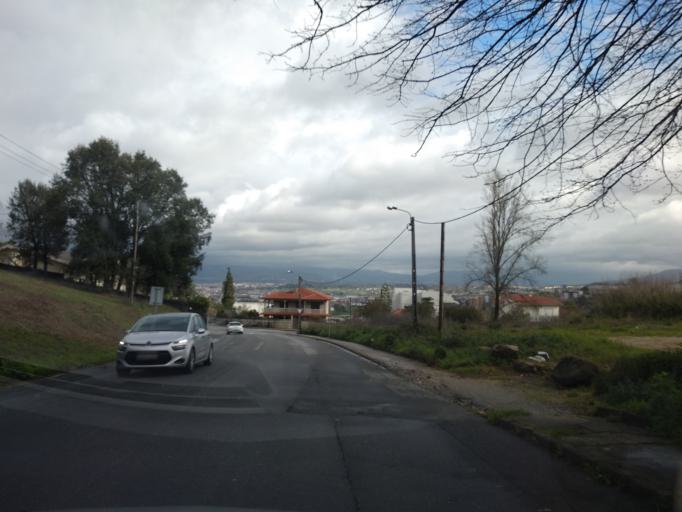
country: PT
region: Braga
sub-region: Braga
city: Braga
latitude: 41.5432
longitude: -8.4426
